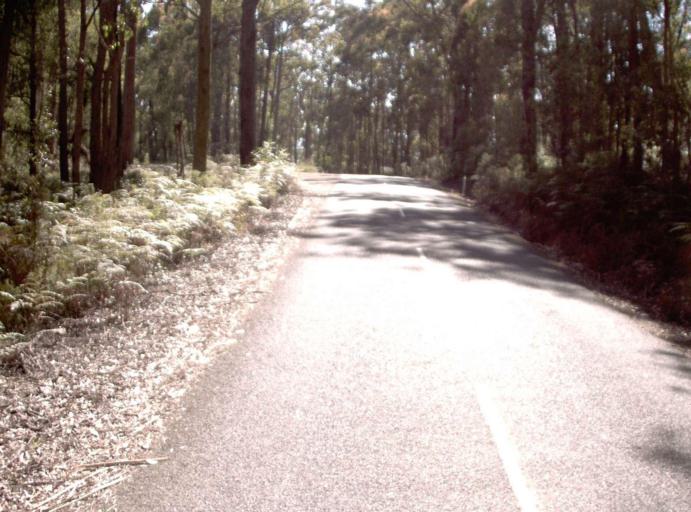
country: AU
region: New South Wales
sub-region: Bombala
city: Bombala
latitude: -37.3872
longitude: 148.6231
